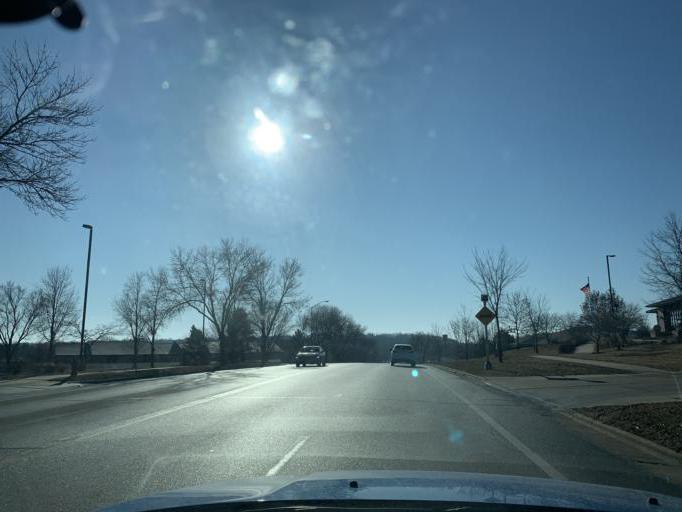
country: US
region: Wisconsin
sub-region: Dane County
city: Verona
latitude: 43.0343
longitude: -89.4969
